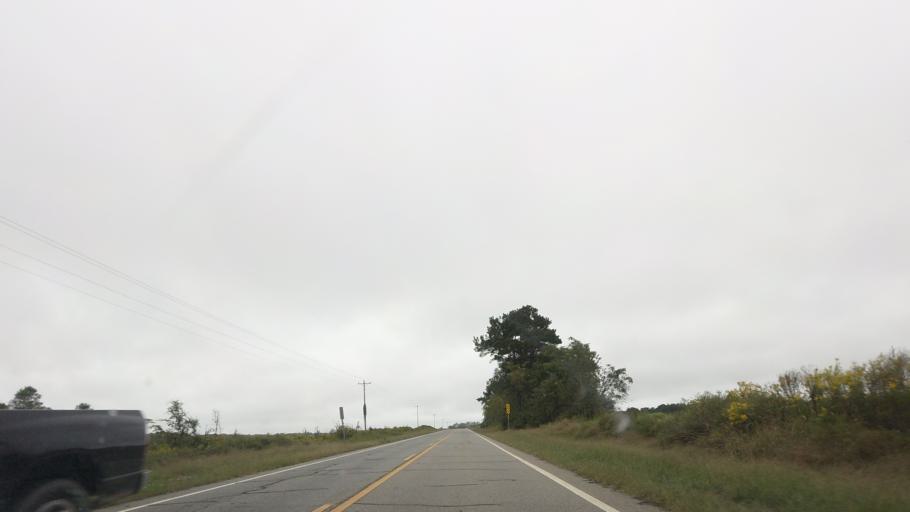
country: US
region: Georgia
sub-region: Irwin County
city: Ocilla
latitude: 31.5168
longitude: -83.2417
